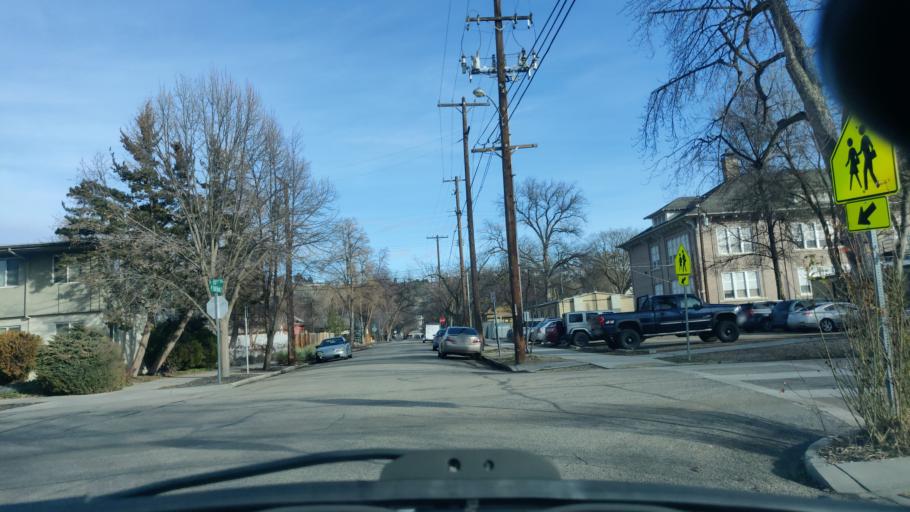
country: US
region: Idaho
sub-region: Ada County
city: Boise
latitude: 43.6284
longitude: -116.2001
